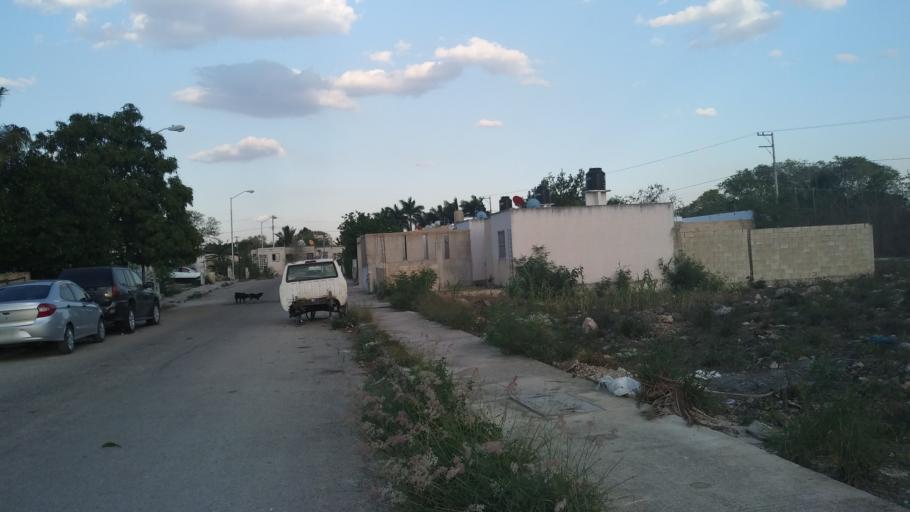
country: MX
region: Yucatan
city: Itzincab Palomeque
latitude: 20.9252
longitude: -89.6682
